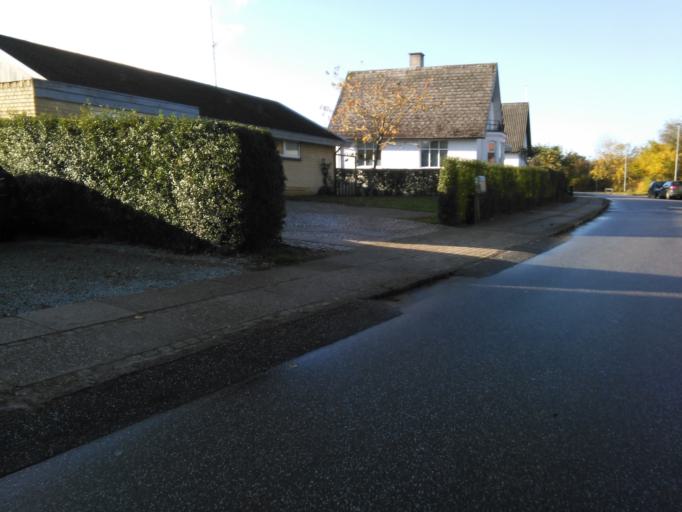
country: DK
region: Central Jutland
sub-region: Arhus Kommune
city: Malling
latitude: 56.0377
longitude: 10.1872
